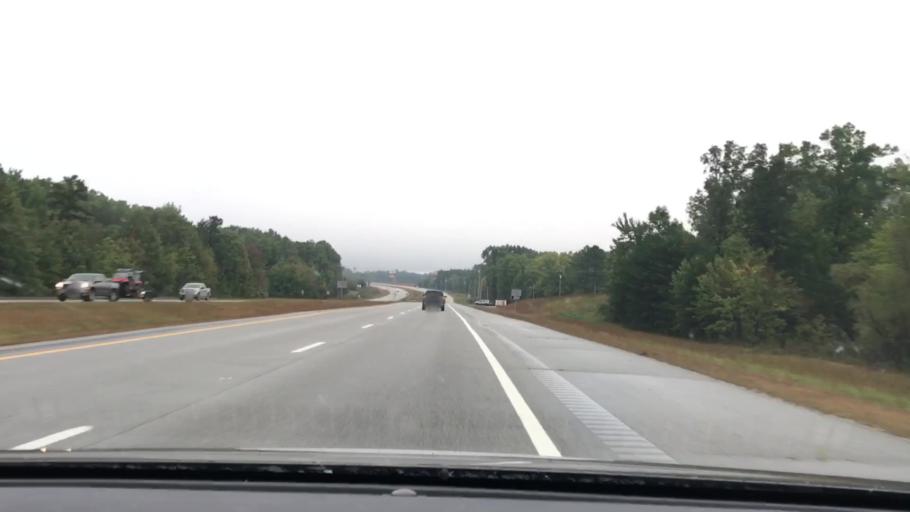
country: US
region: Tennessee
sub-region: Fentress County
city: Grimsley
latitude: 36.3339
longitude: -84.9568
